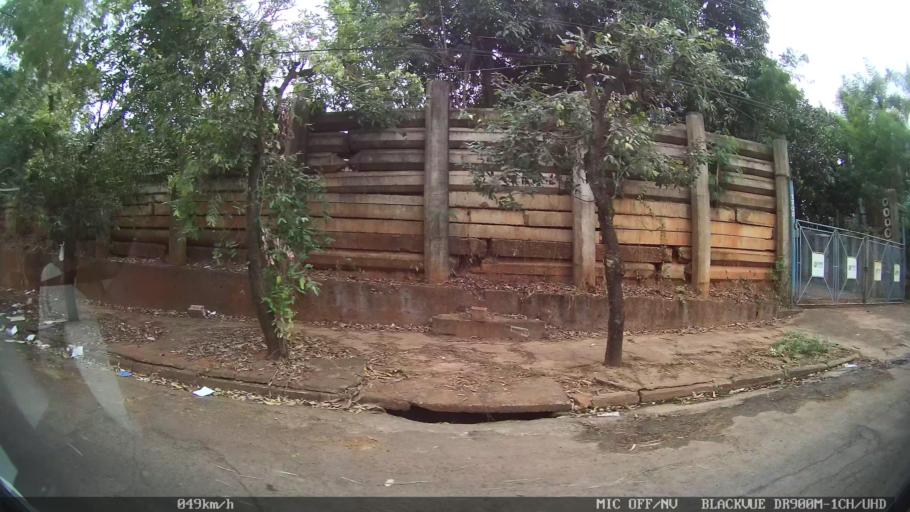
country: BR
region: Sao Paulo
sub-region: Sao Jose Do Rio Preto
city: Sao Jose do Rio Preto
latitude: -20.8176
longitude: -49.4321
